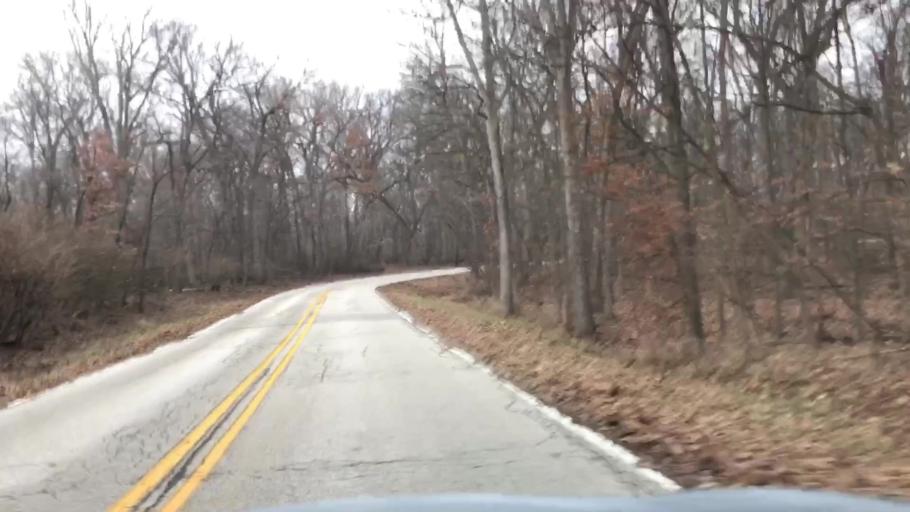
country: US
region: Illinois
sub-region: McLean County
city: Hudson
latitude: 40.6430
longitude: -88.9140
